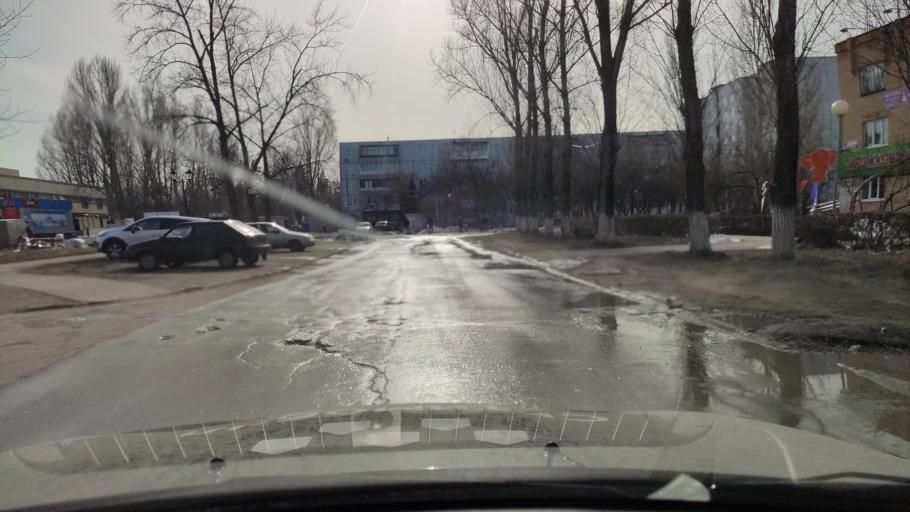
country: RU
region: Samara
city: Povolzhskiy
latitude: 53.5860
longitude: 49.7620
